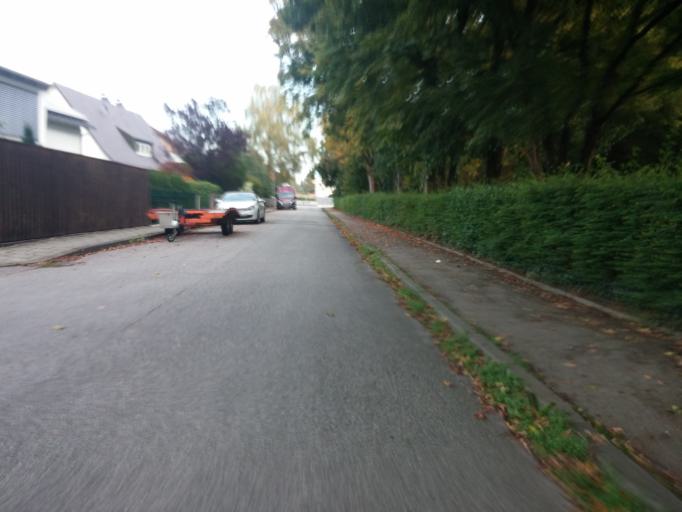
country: DE
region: Bavaria
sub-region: Upper Bavaria
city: Vaterstetten
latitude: 48.0957
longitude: 11.7632
